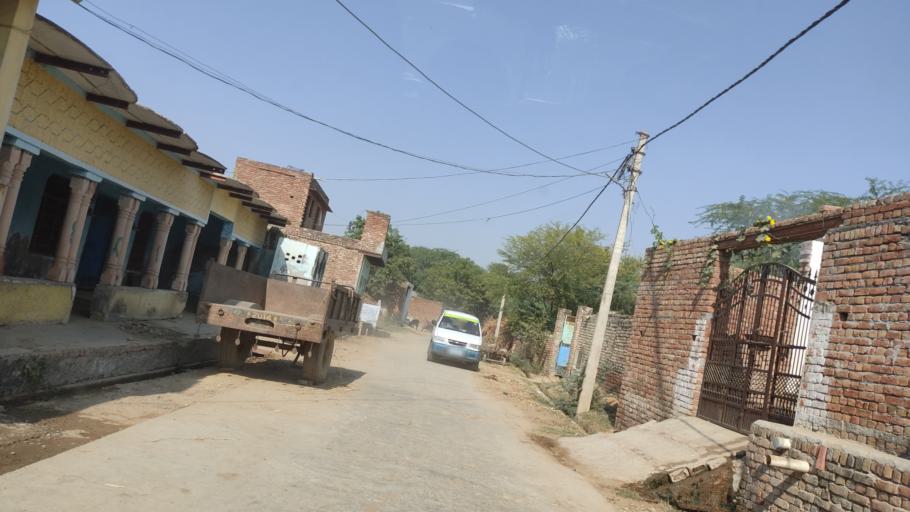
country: IN
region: Uttar Pradesh
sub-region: Mathura
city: Radha Kund
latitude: 27.5113
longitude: 77.4978
